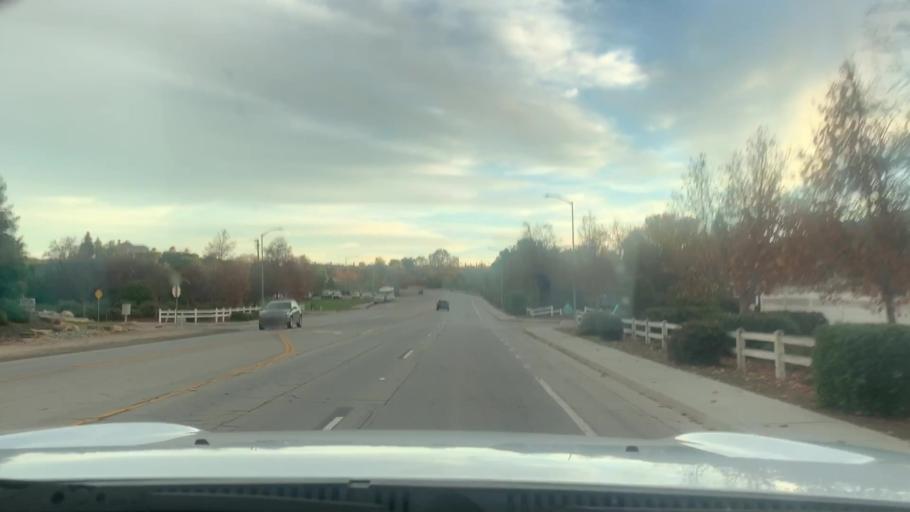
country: US
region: California
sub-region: San Luis Obispo County
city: Paso Robles
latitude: 35.6373
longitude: -120.6582
